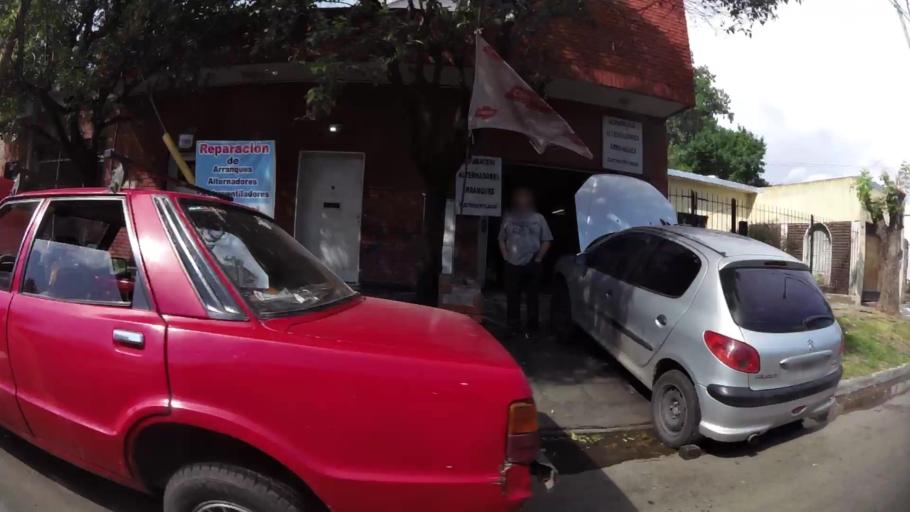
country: AR
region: Buenos Aires
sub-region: Partido de Merlo
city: Merlo
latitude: -34.6394
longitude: -58.6983
